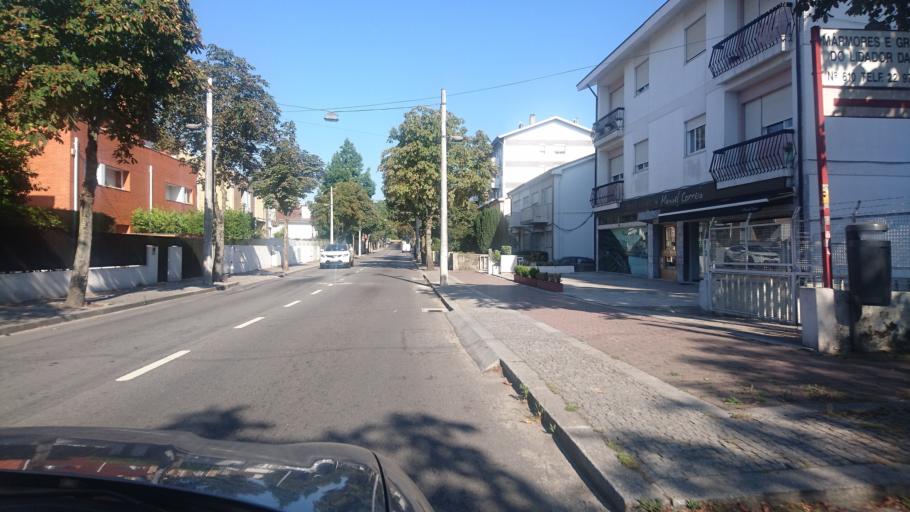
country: PT
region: Porto
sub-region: Valongo
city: Ermesinde
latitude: 41.2054
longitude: -8.5605
